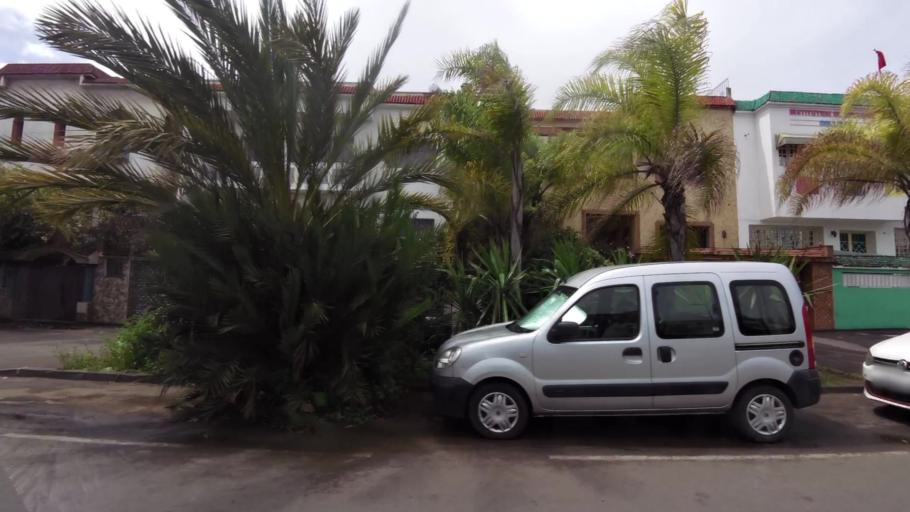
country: MA
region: Grand Casablanca
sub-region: Casablanca
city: Casablanca
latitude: 33.5556
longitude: -7.6817
